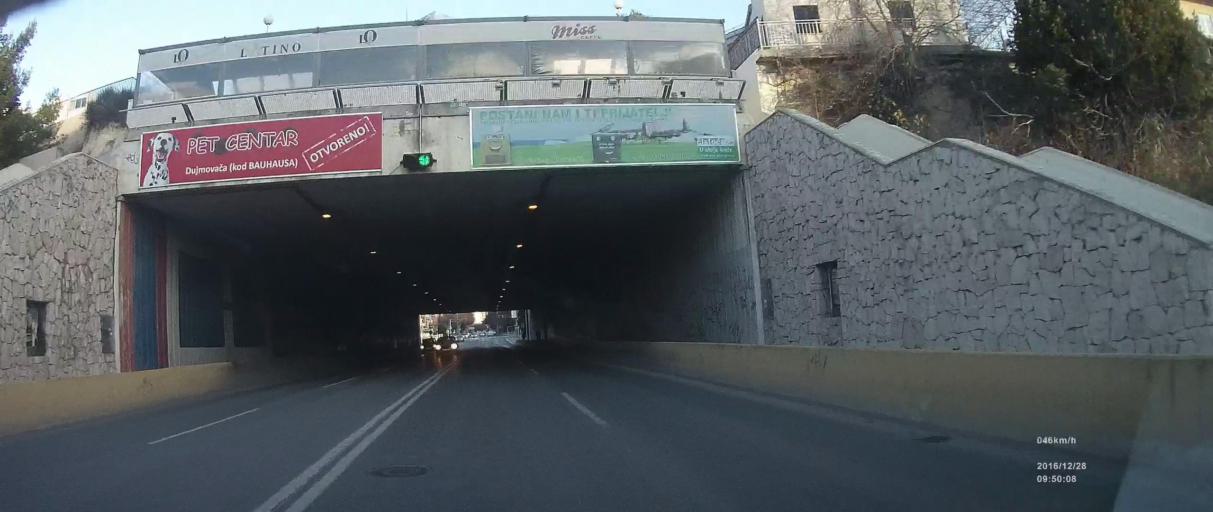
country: HR
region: Splitsko-Dalmatinska
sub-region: Grad Split
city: Split
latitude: 43.5073
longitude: 16.4558
